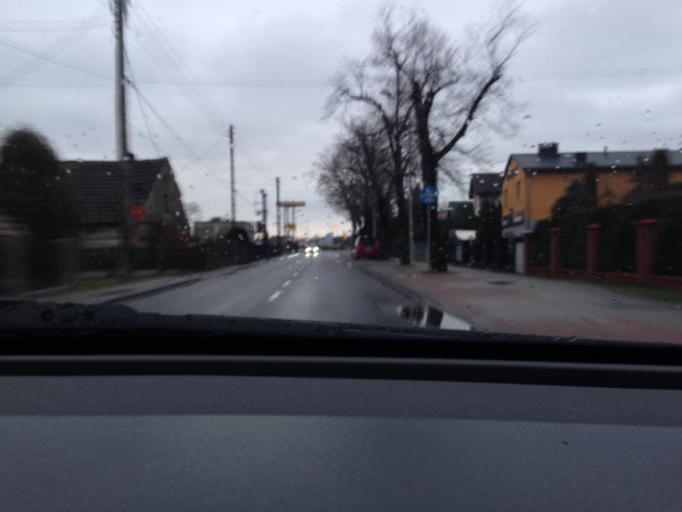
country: PL
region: Opole Voivodeship
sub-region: Powiat opolski
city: Opole
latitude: 50.6781
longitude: 17.9593
